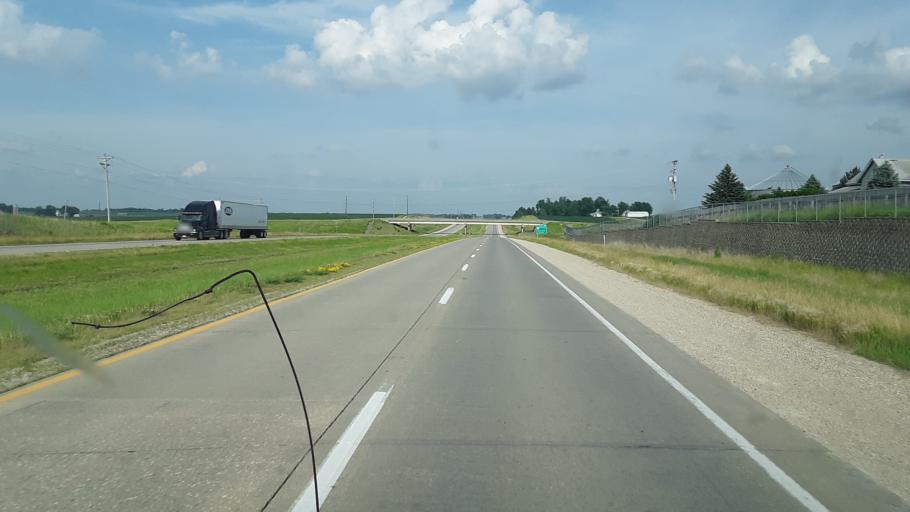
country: US
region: Iowa
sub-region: Marshall County
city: Marshalltown
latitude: 42.0076
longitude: -93.0045
